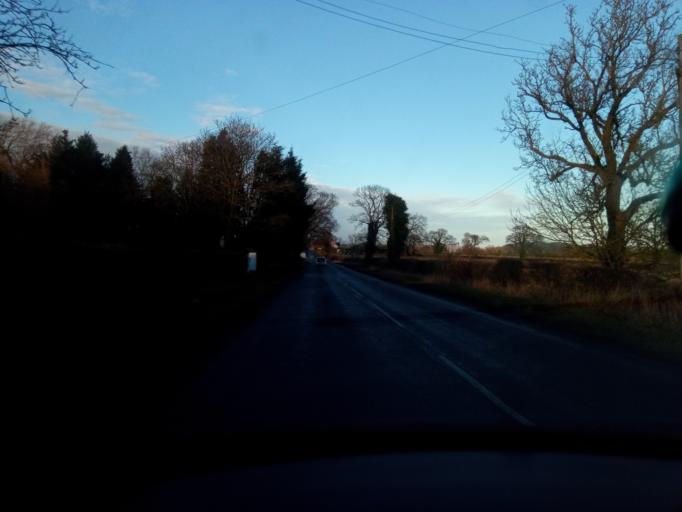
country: GB
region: England
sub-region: Darlington
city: High Coniscliffe
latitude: 54.5149
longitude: -1.6715
